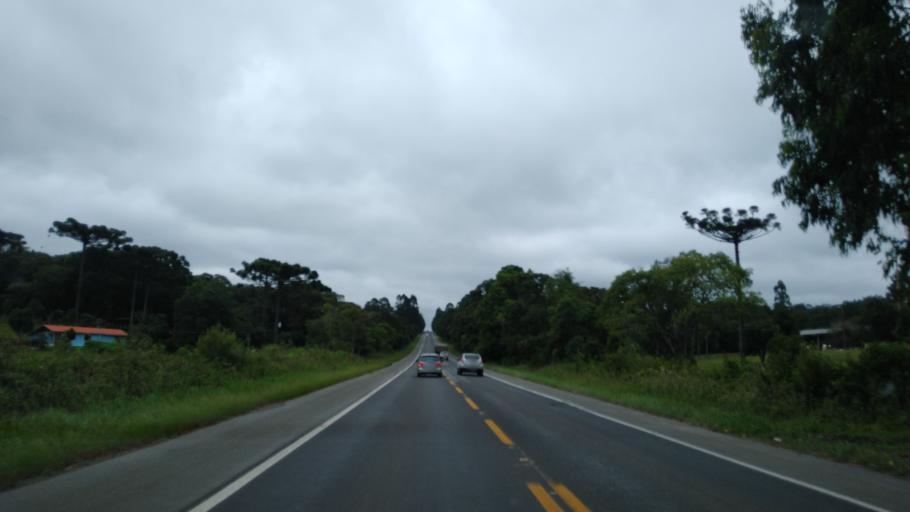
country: BR
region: Santa Catarina
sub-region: Tres Barras
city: Tres Barras
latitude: -26.1831
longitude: -50.2110
